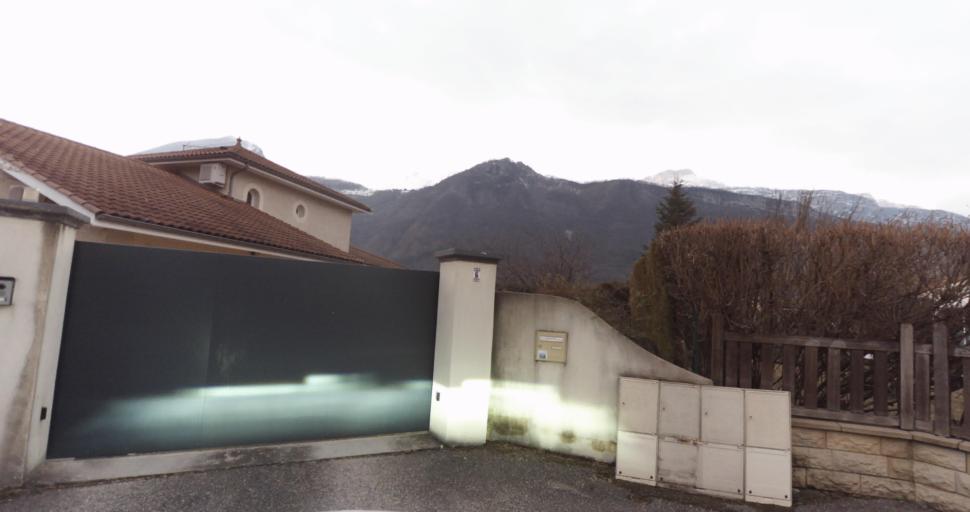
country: FR
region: Rhone-Alpes
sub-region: Departement de l'Isere
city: Vif
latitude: 45.0634
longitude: 5.6788
